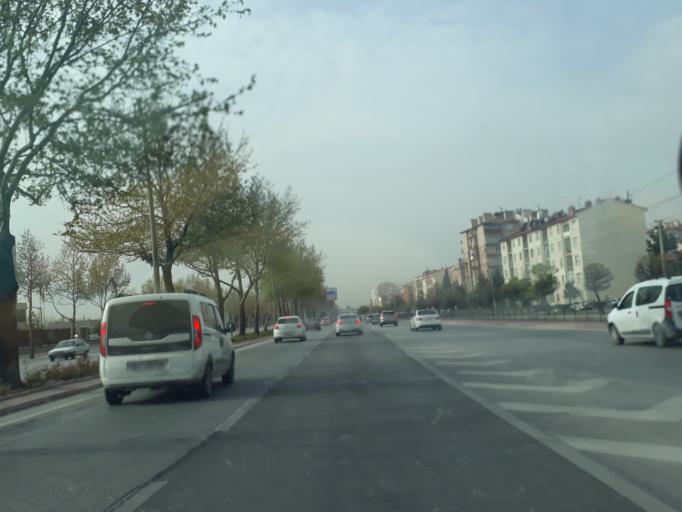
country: TR
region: Konya
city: Selcuklu
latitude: 37.9460
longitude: 32.5124
